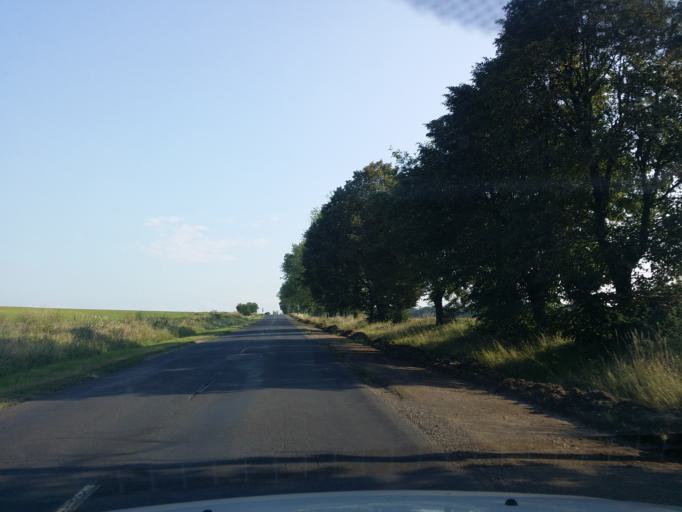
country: HU
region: Borsod-Abauj-Zemplen
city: Abaujszanto
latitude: 48.3709
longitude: 21.2155
